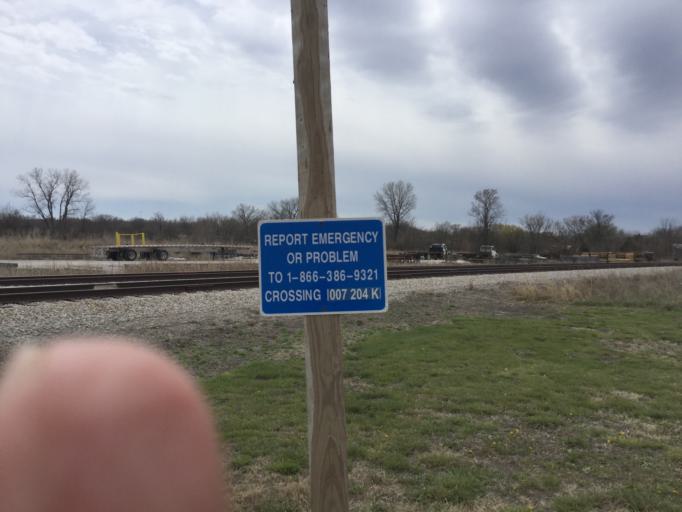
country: US
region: Kansas
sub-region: Wilson County
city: Fredonia
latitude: 37.5446
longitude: -95.8250
